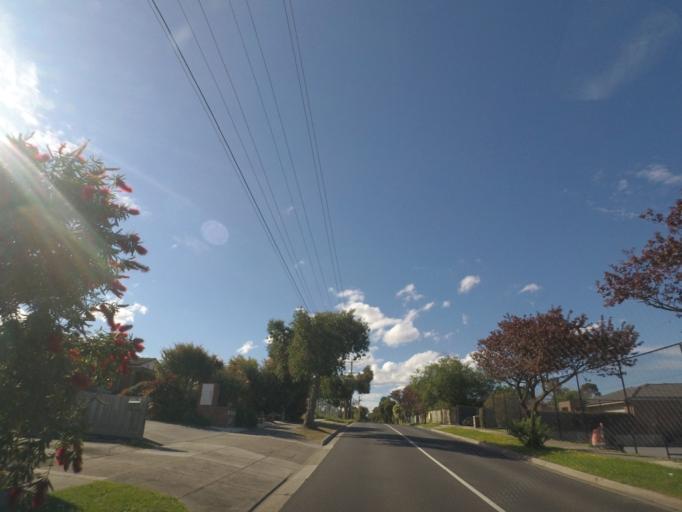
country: AU
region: Victoria
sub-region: Knox
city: Knoxfield
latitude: -37.8941
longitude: 145.2490
